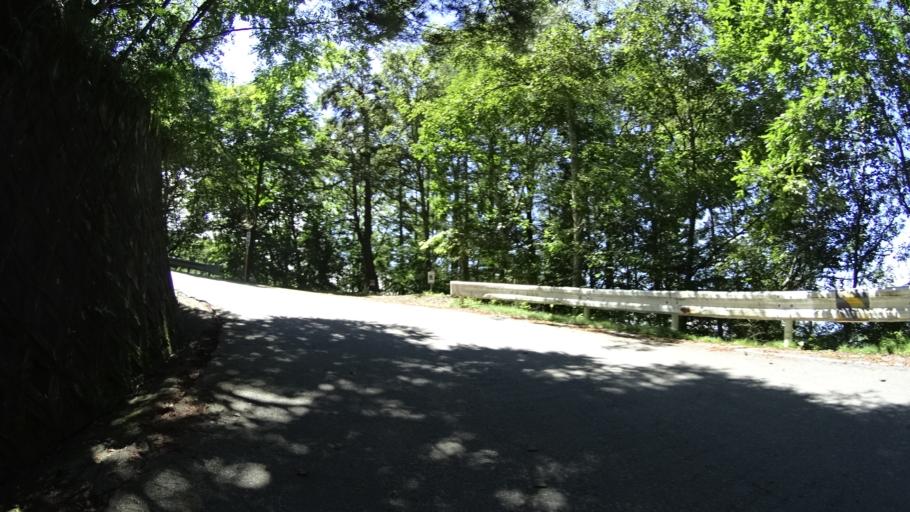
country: JP
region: Yamanashi
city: Enzan
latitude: 35.7430
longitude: 138.8217
